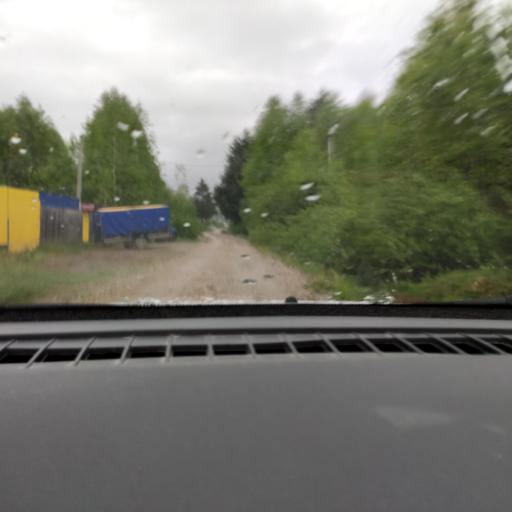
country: RU
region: Perm
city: Kondratovo
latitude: 58.0510
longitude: 56.0159
